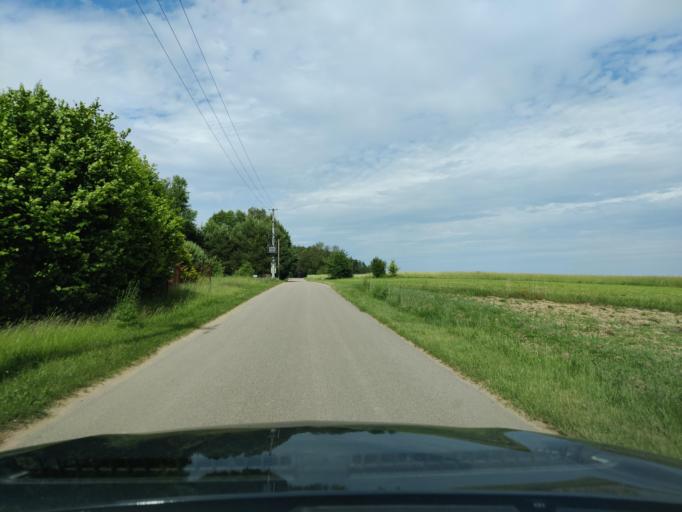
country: PL
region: Masovian Voivodeship
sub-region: Powiat pultuski
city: Obryte
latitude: 52.7489
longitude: 21.1972
